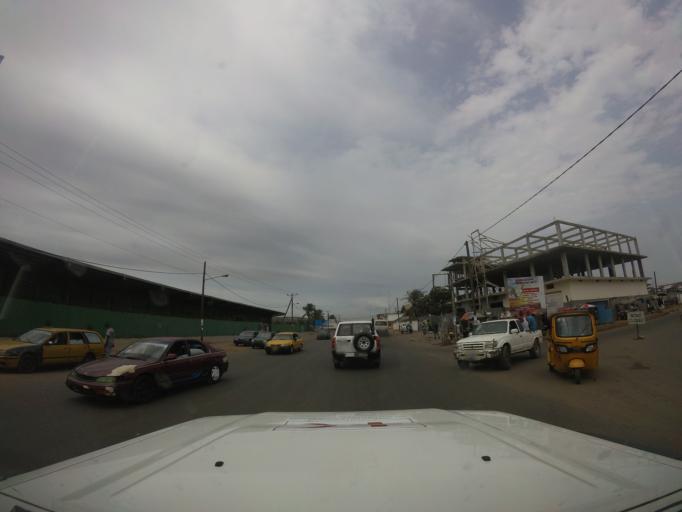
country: LR
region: Montserrado
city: Monrovia
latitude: 6.3442
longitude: -10.7900
